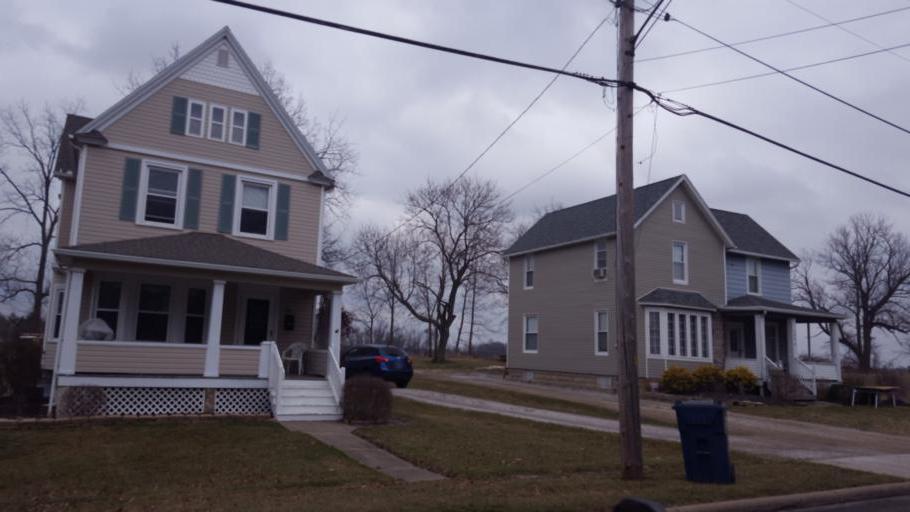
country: US
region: Ohio
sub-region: Richland County
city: Shelby
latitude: 40.8809
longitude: -82.6476
